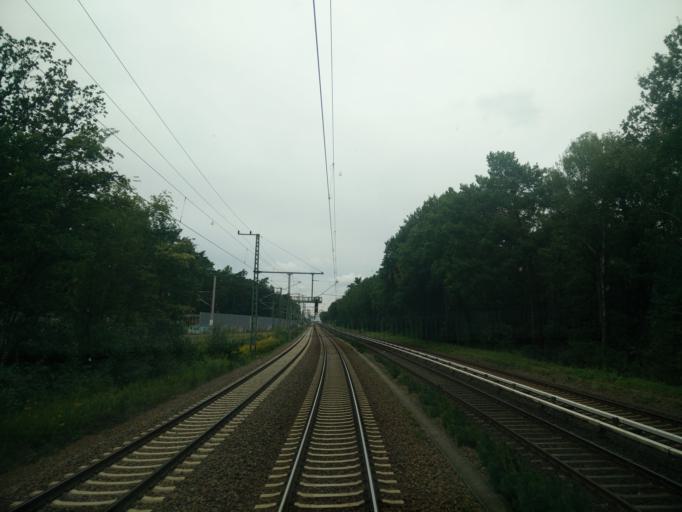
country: DE
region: Berlin
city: Bohnsdorf
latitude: 52.3965
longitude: 13.5978
